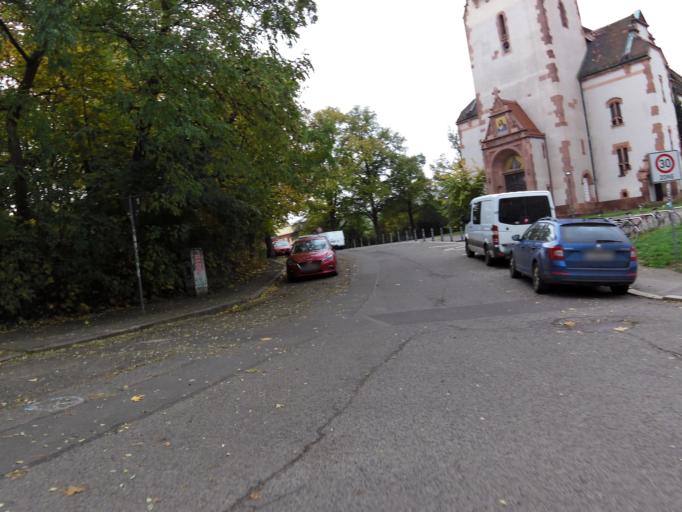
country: DE
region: Saxony
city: Leipzig
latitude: 51.3095
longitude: 12.3720
